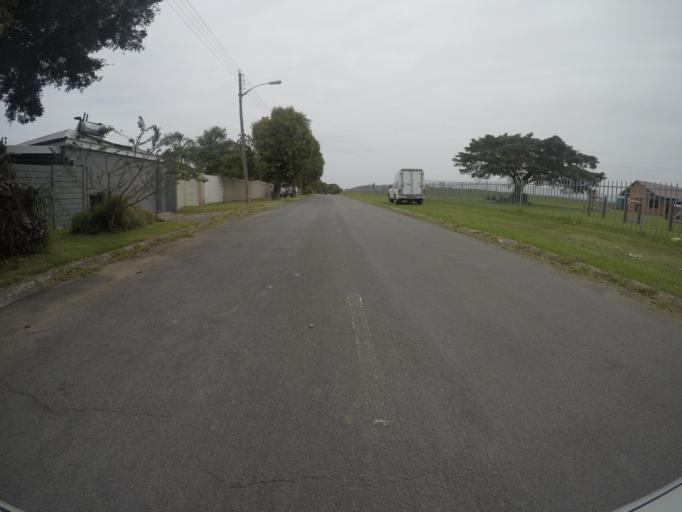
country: ZA
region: Eastern Cape
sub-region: Buffalo City Metropolitan Municipality
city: East London
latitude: -32.9675
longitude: 27.9373
